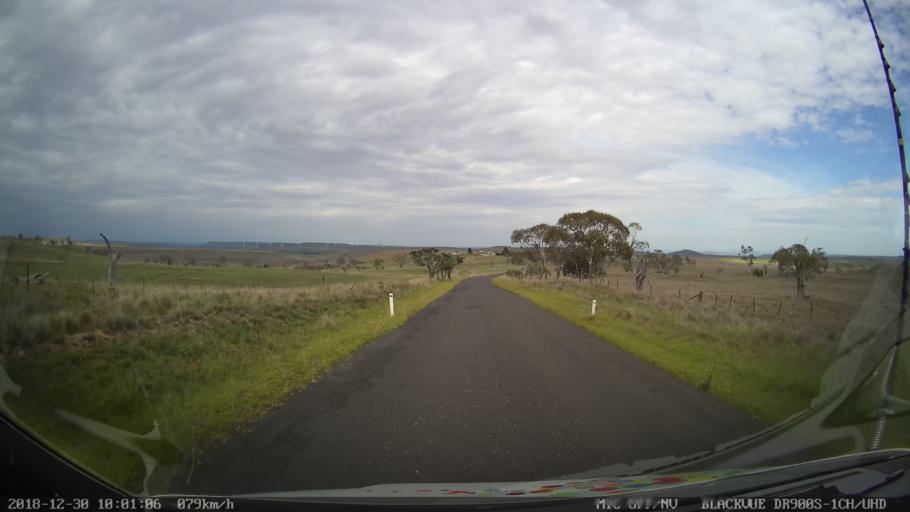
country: AU
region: New South Wales
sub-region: Cooma-Monaro
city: Cooma
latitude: -36.5141
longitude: 149.1910
